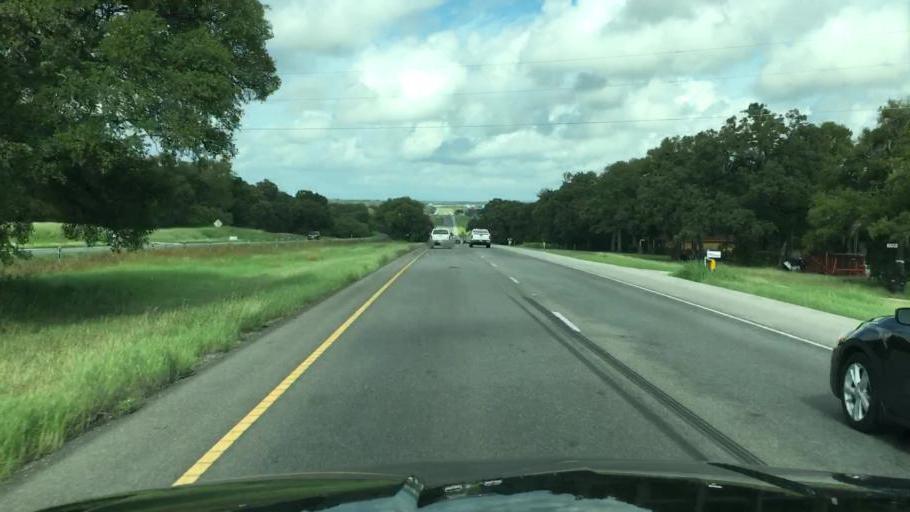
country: US
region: Texas
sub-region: Bastrop County
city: Wyldwood
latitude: 30.1527
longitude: -97.4906
